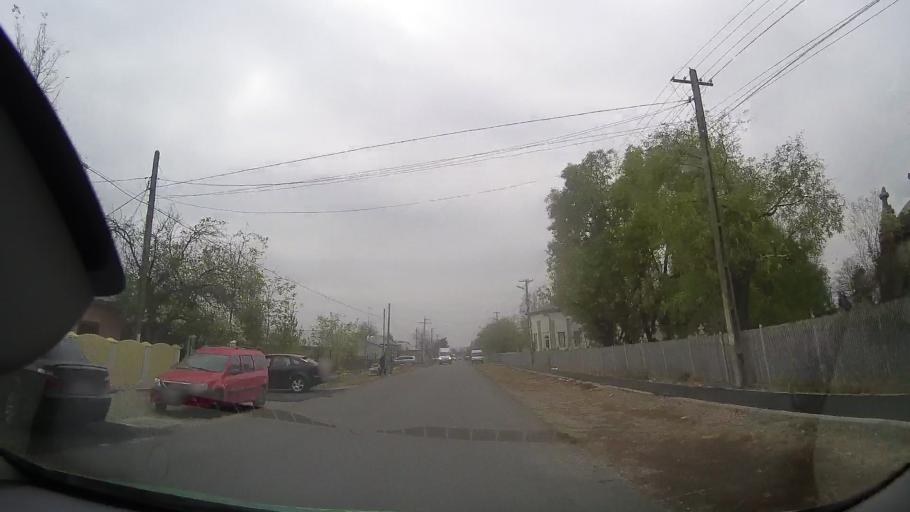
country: RO
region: Buzau
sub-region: Comuna Pogoanele
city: Pogoanele
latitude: 44.9248
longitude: 26.9951
